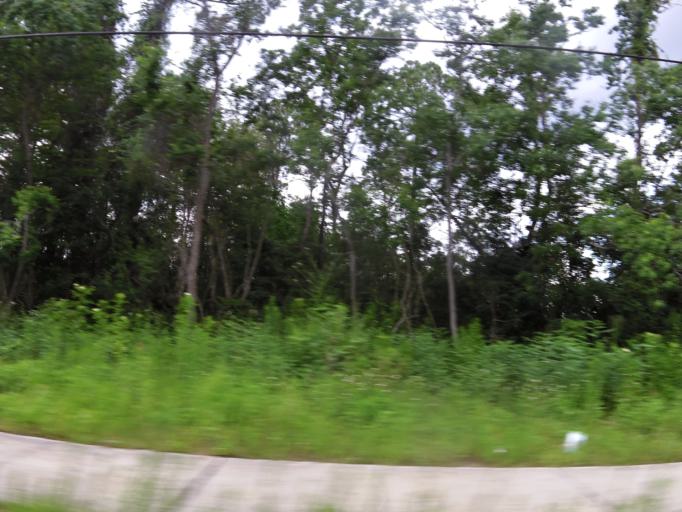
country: US
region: Florida
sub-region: Duval County
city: Jacksonville
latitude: 30.4104
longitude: -81.6613
